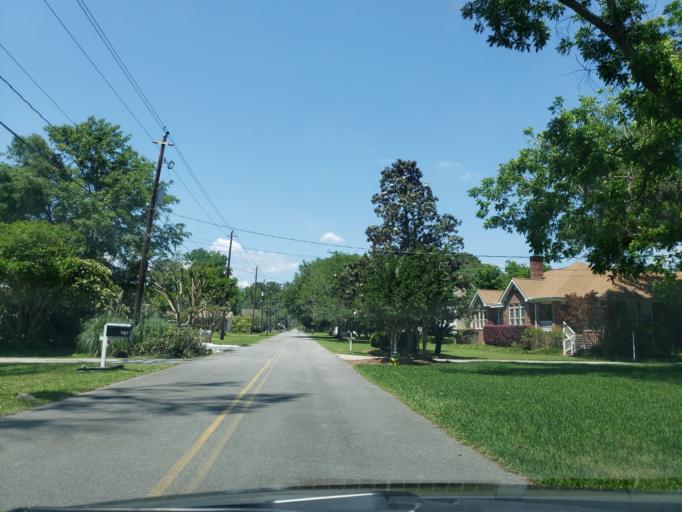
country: US
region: Georgia
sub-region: Chatham County
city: Isle of Hope
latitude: 31.9825
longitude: -81.0626
